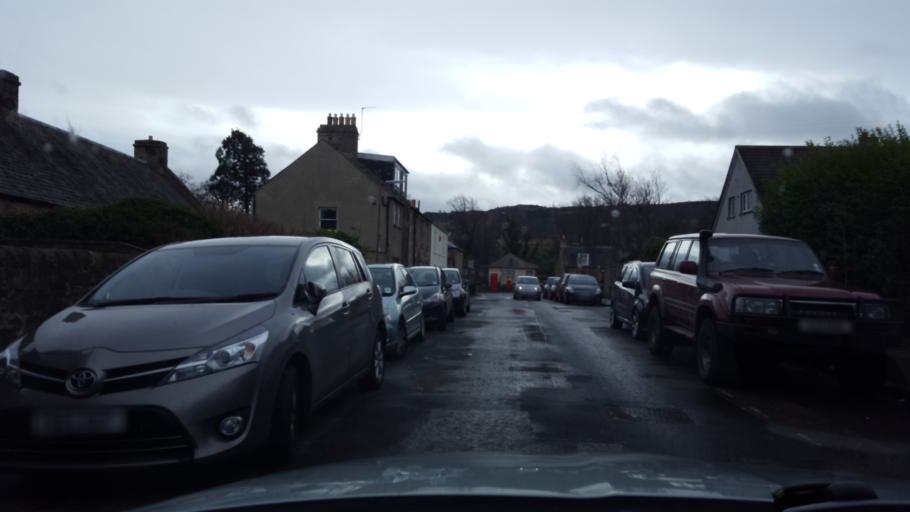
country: GB
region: Scotland
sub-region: Edinburgh
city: Currie
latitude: 55.9041
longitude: -3.2855
